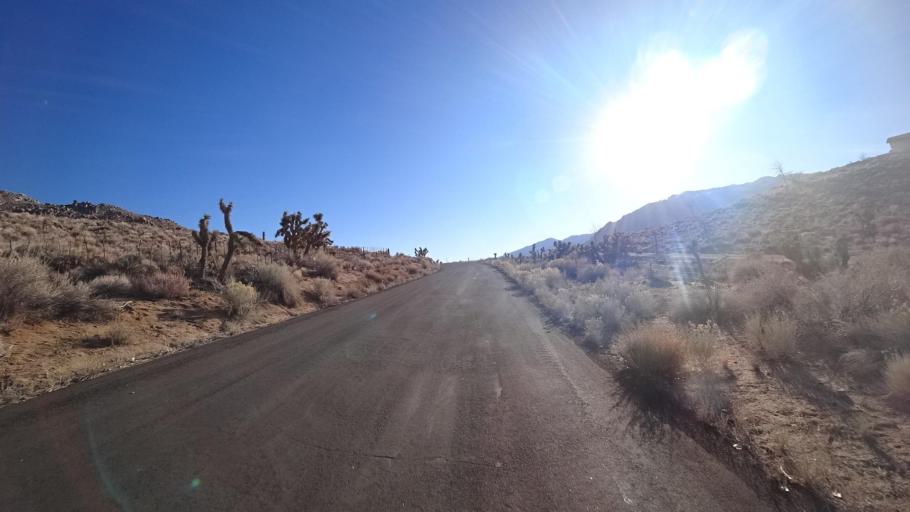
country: US
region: California
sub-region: Kern County
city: Weldon
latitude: 35.5074
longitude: -118.2036
